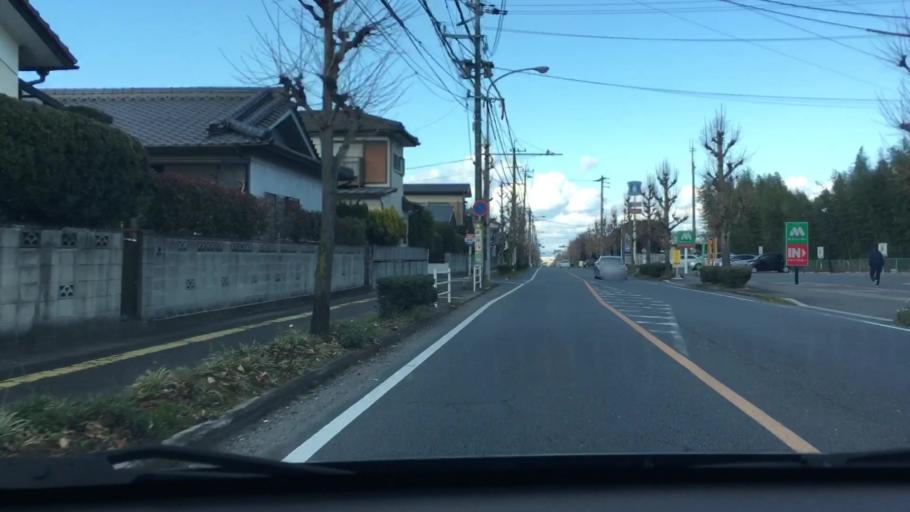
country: JP
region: Oita
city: Tsurusaki
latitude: 33.2134
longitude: 131.6588
